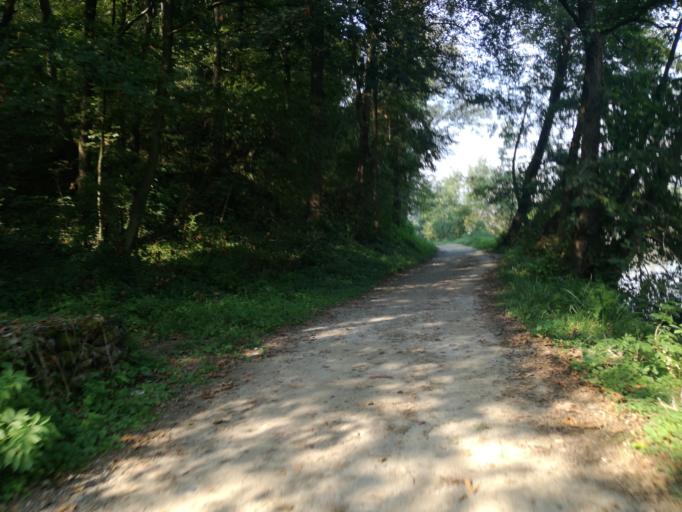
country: IT
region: Lombardy
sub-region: Provincia di Lecco
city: Arlate
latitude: 45.7235
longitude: 9.4481
